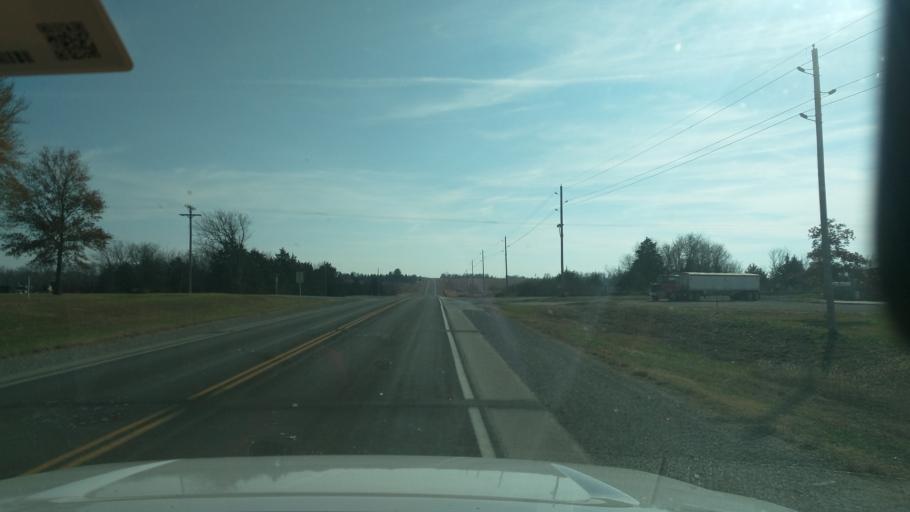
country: US
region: Kansas
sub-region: Lyon County
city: Emporia
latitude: 38.3479
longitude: -96.1803
